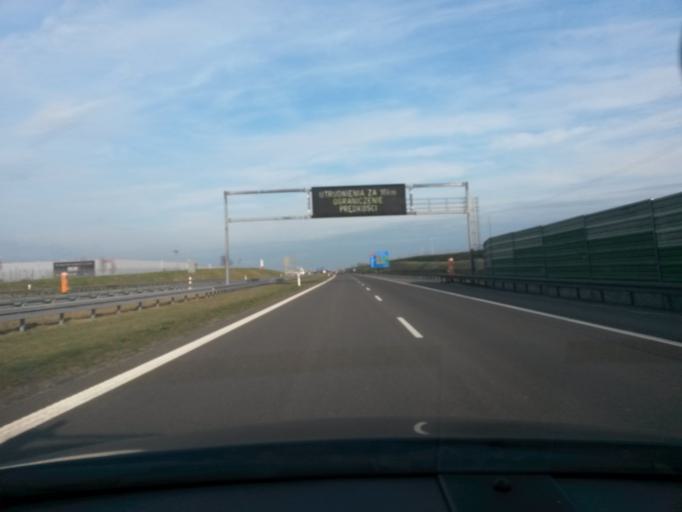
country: PL
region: Lodz Voivodeship
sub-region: Powiat zgierski
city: Strykow
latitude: 51.8902
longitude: 19.5711
